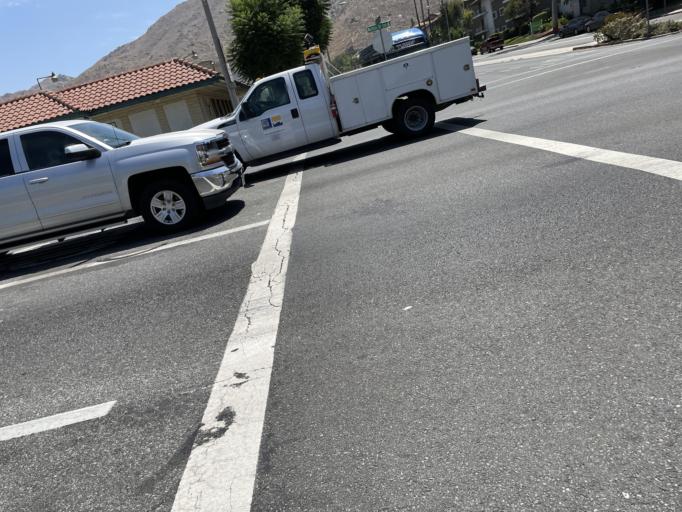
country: US
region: California
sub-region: Riverside County
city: Highgrove
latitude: 33.9758
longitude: -117.3165
